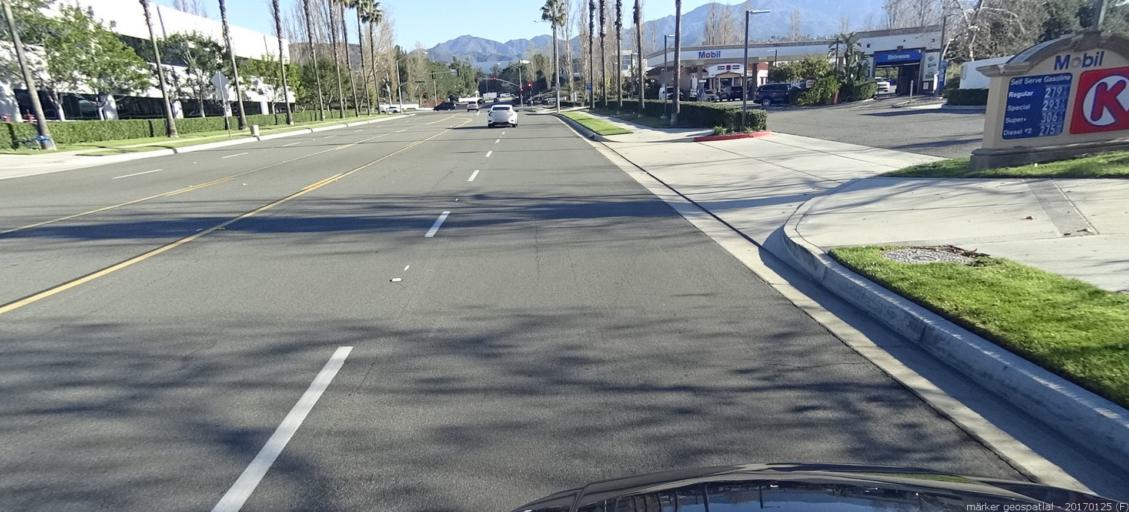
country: US
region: California
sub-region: Orange County
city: Foothill Ranch
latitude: 33.6723
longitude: -117.6566
